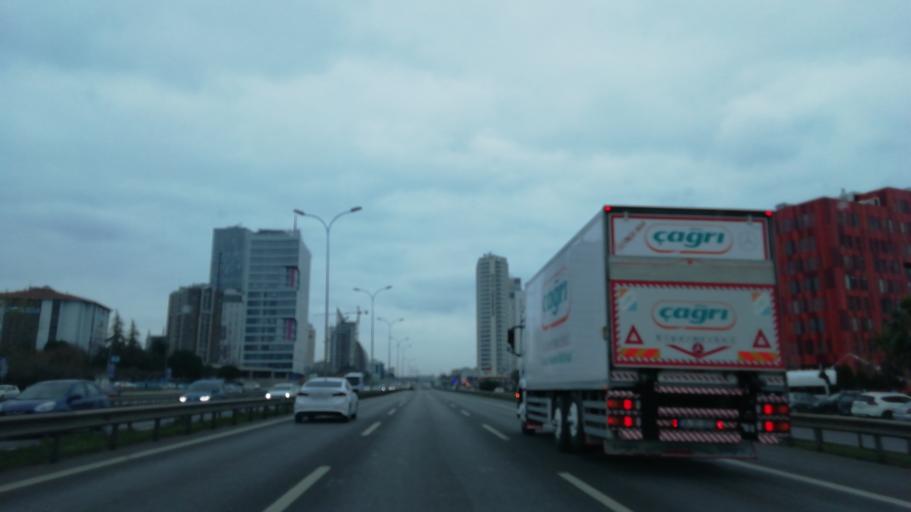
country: TR
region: Istanbul
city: Maltepe
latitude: 40.9126
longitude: 29.1918
